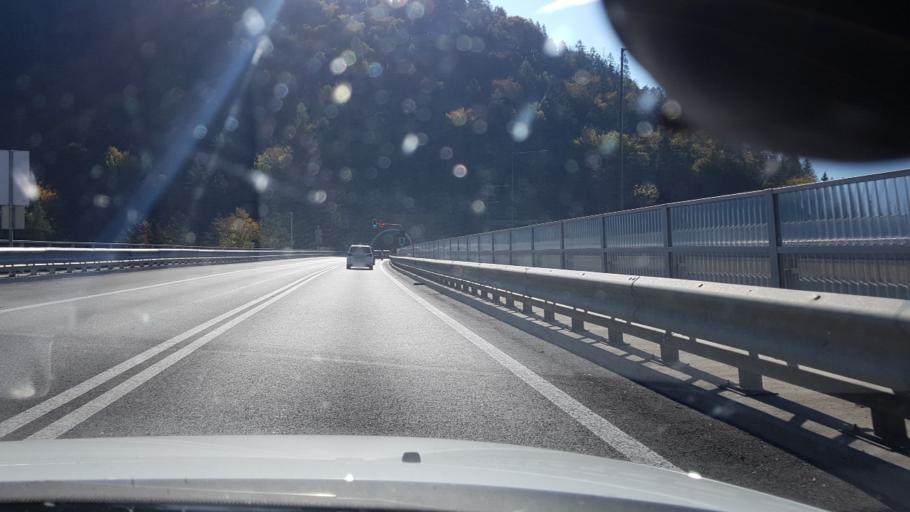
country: AT
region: Upper Austria
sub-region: Politischer Bezirk Kirchdorf an der Krems
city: Micheldorf in Oberoesterreich
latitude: 47.8181
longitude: 14.1694
